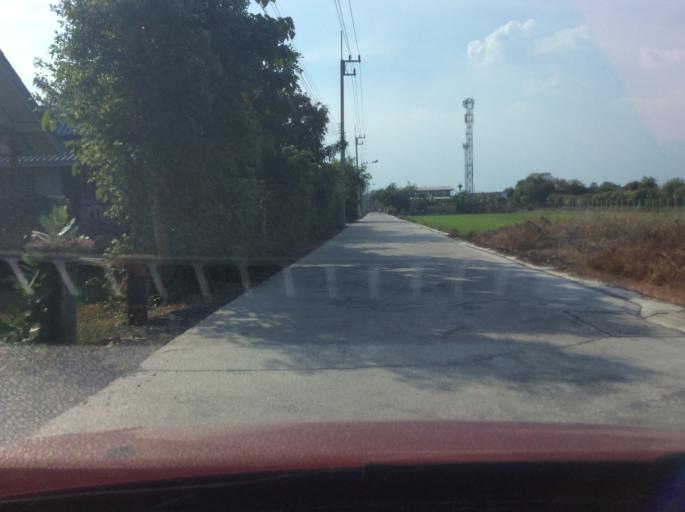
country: TH
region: Pathum Thani
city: Lam Luk Ka
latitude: 13.9677
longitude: 100.7318
